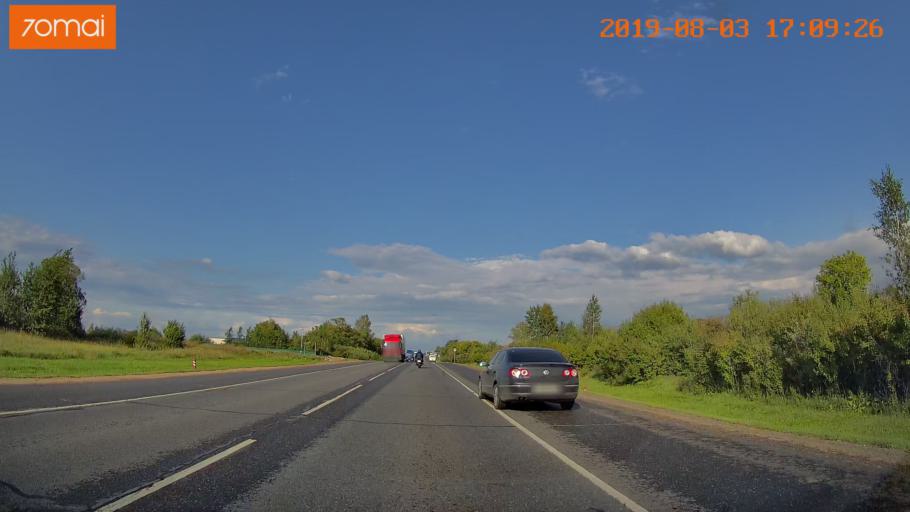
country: RU
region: Moskovskaya
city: Troitskoye
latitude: 55.3041
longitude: 38.5886
